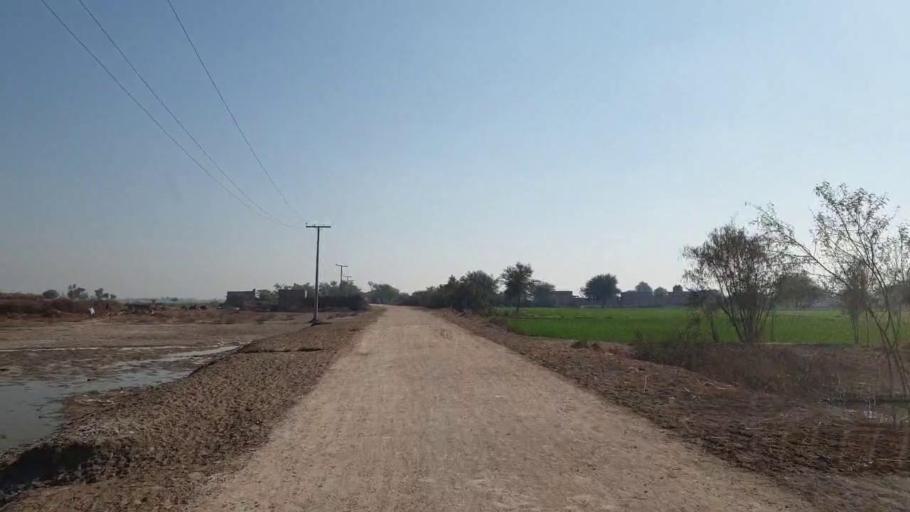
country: PK
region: Sindh
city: Nawabshah
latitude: 26.0819
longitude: 68.4772
